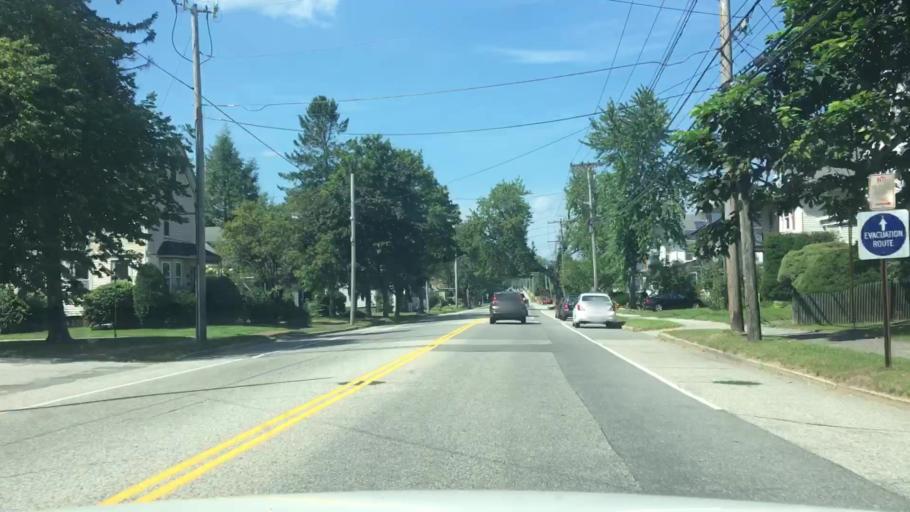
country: US
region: Maine
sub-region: Cumberland County
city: Portland
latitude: 43.6869
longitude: -70.2701
